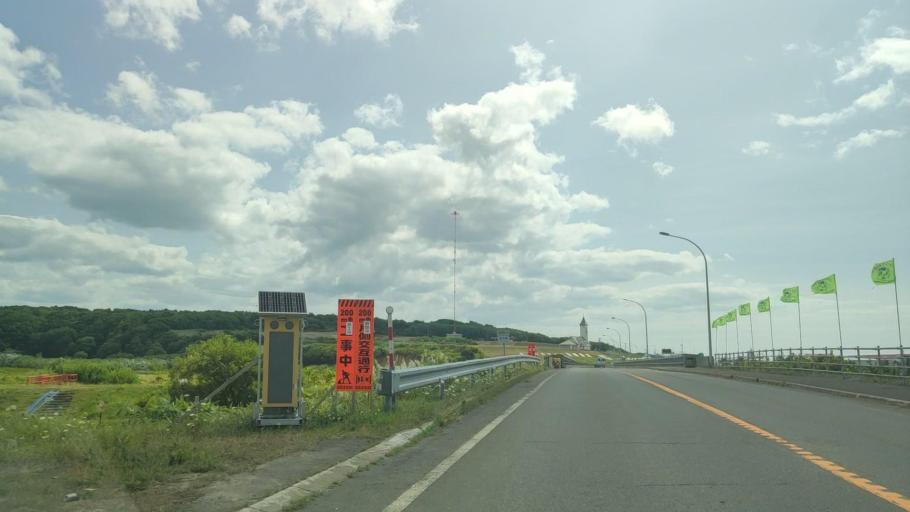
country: JP
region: Hokkaido
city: Makubetsu
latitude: 44.7188
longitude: 141.7933
